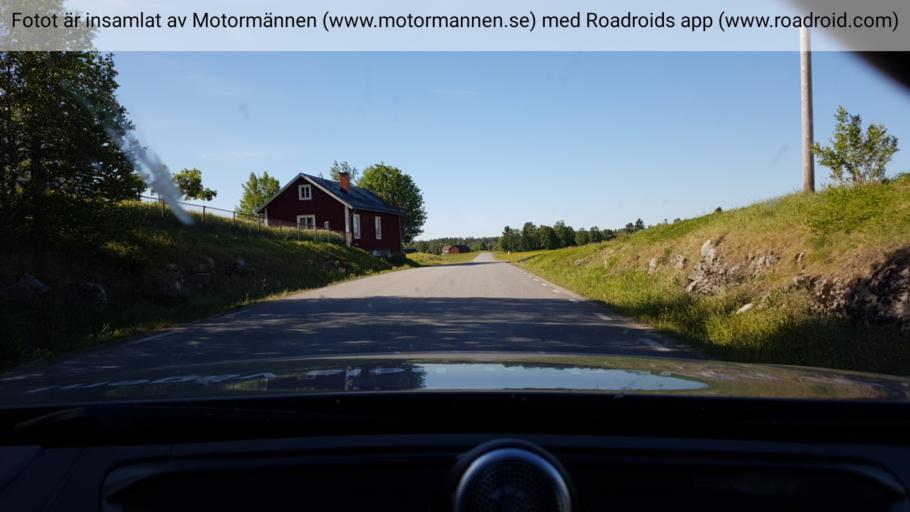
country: SE
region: Jaemtland
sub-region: OEstersunds Kommun
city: Brunflo
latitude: 63.0159
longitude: 14.7345
